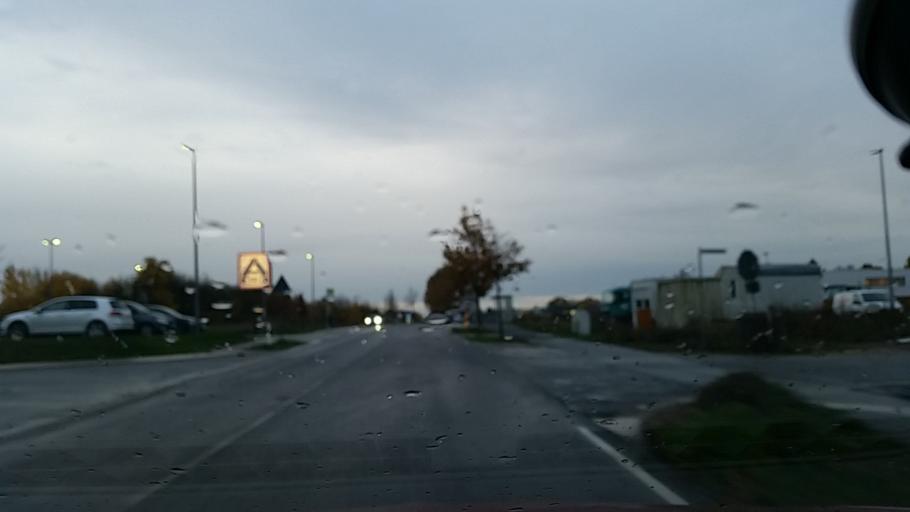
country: DE
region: Lower Saxony
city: Ruhen
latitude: 52.4647
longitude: 10.8516
